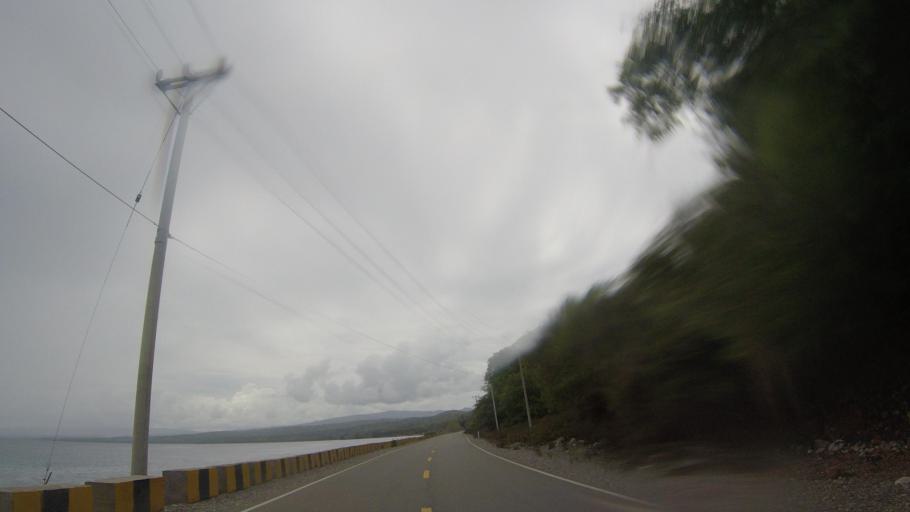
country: TL
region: Lautem
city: Lospalos
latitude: -8.4149
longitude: 126.7464
